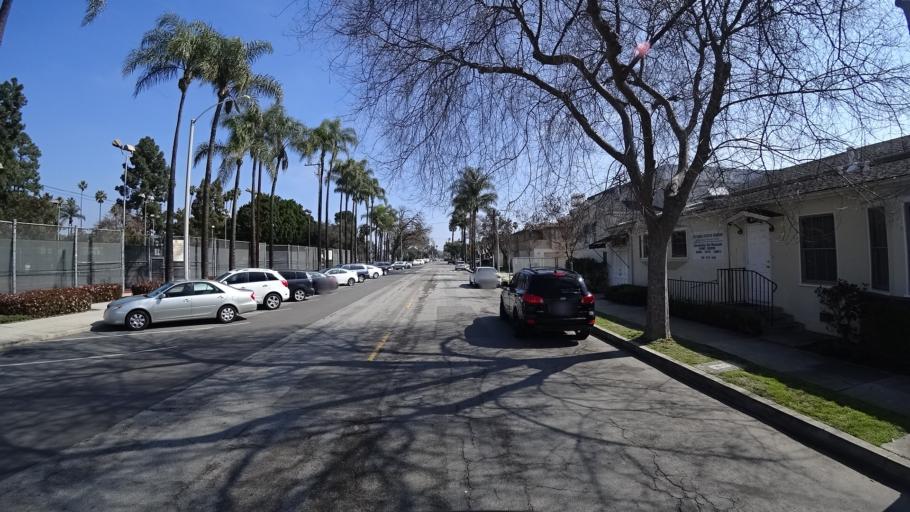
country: US
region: California
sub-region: Orange County
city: Anaheim
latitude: 33.8367
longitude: -117.9189
